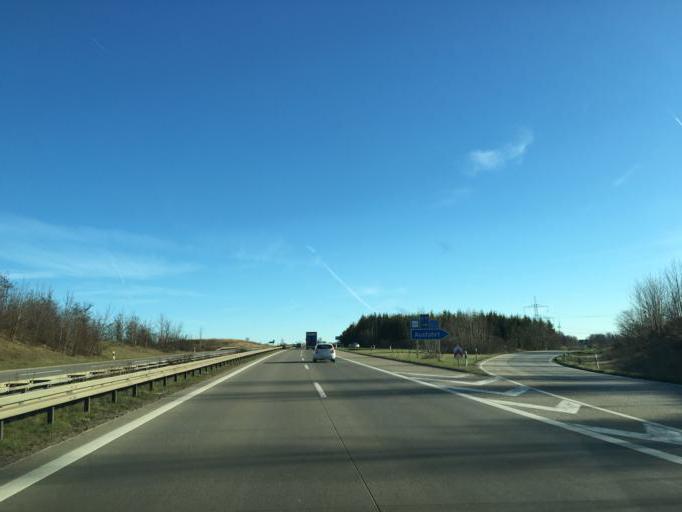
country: DE
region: Mecklenburg-Vorpommern
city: Roggentin
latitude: 54.0535
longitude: 12.1980
